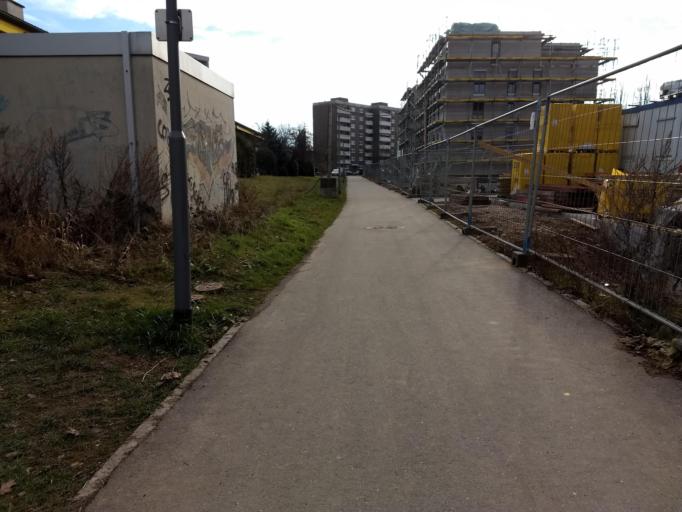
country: DE
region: Baden-Wuerttemberg
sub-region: Freiburg Region
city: Weil am Rhein
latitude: 47.5985
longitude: 7.6229
